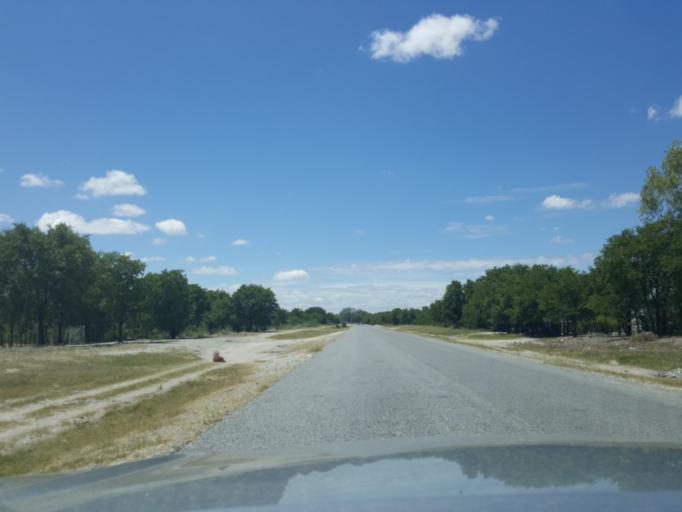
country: BW
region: Central
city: Nata
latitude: -20.2129
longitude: 26.1728
